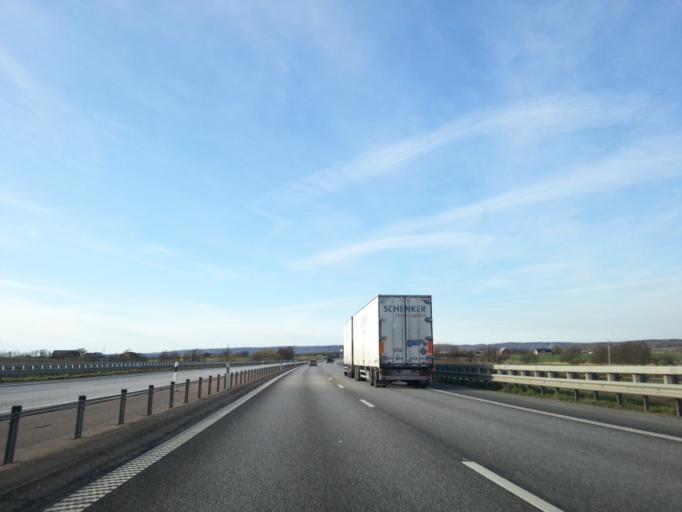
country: SE
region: Skane
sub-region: Angelholms Kommun
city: AEngelholm
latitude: 56.2652
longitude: 12.8941
